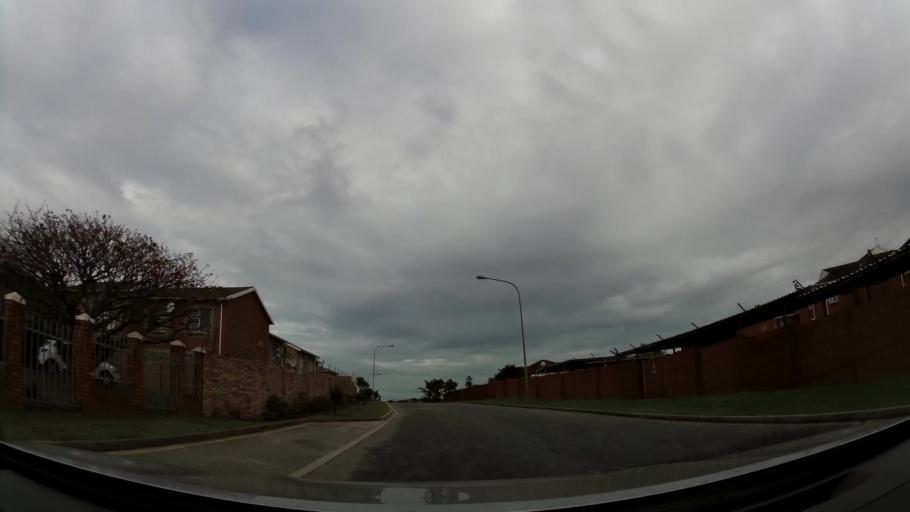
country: ZA
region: Eastern Cape
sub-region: Nelson Mandela Bay Metropolitan Municipality
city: Port Elizabeth
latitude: -33.9702
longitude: 25.6219
